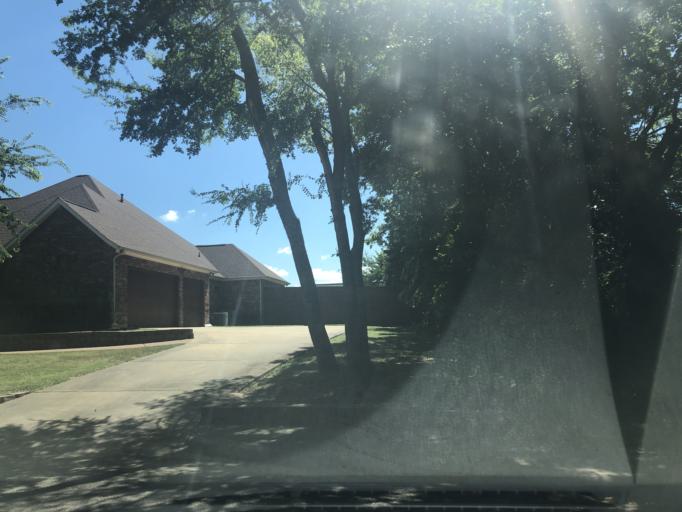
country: US
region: Texas
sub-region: Dallas County
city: Duncanville
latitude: 32.6468
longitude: -96.9274
